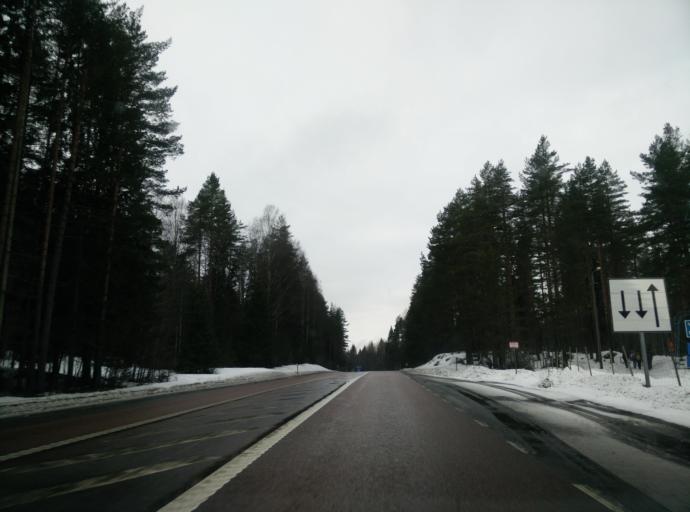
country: SE
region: Gaevleborg
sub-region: Hofors Kommun
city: Hofors
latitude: 60.5607
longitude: 16.3316
